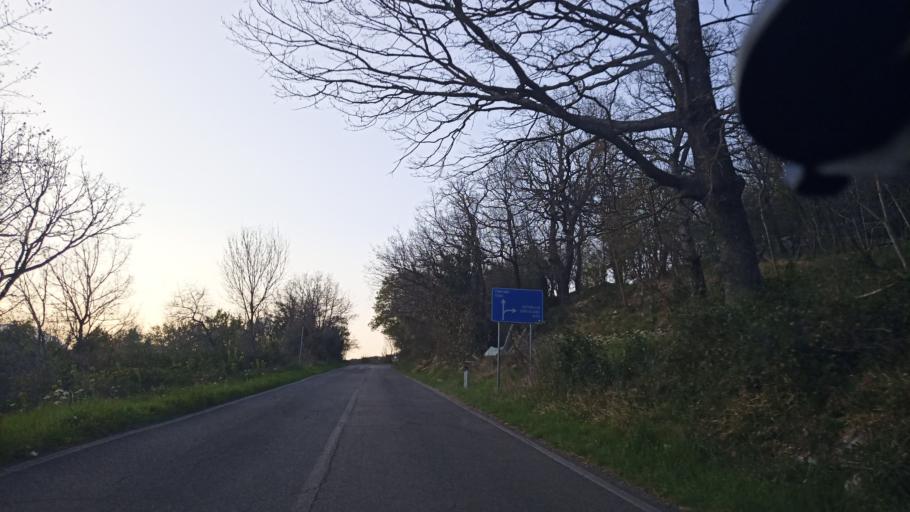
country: IT
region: Latium
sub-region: Provincia di Rieti
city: Cottanello
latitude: 42.4115
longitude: 12.6795
